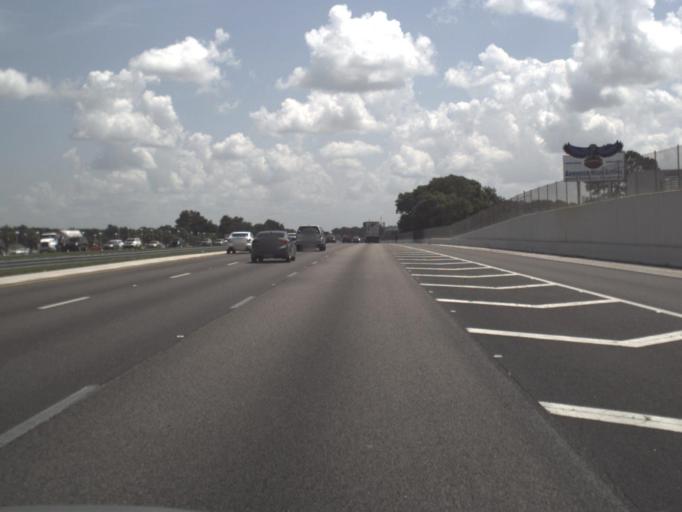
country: US
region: Florida
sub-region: Hillsborough County
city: Mango
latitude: 28.0066
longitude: -82.2988
